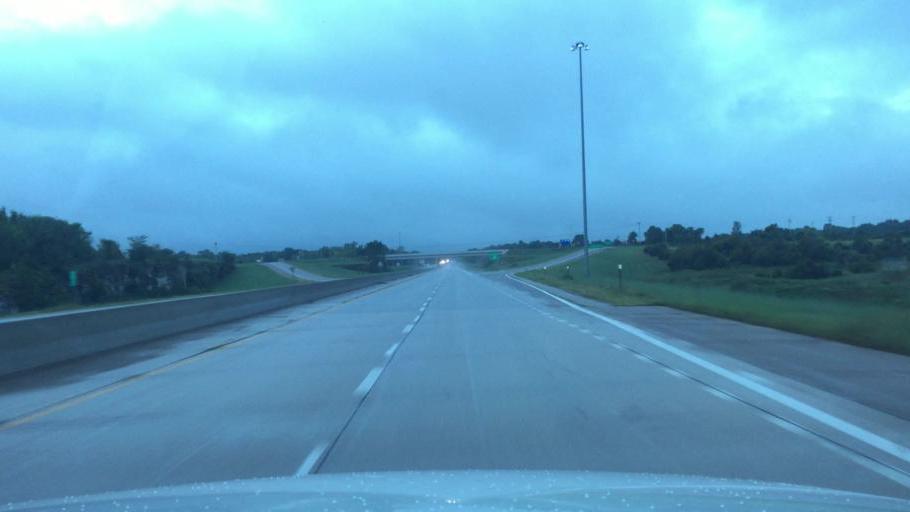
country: US
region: Kansas
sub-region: Neosho County
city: Chanute
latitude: 37.6931
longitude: -95.4796
